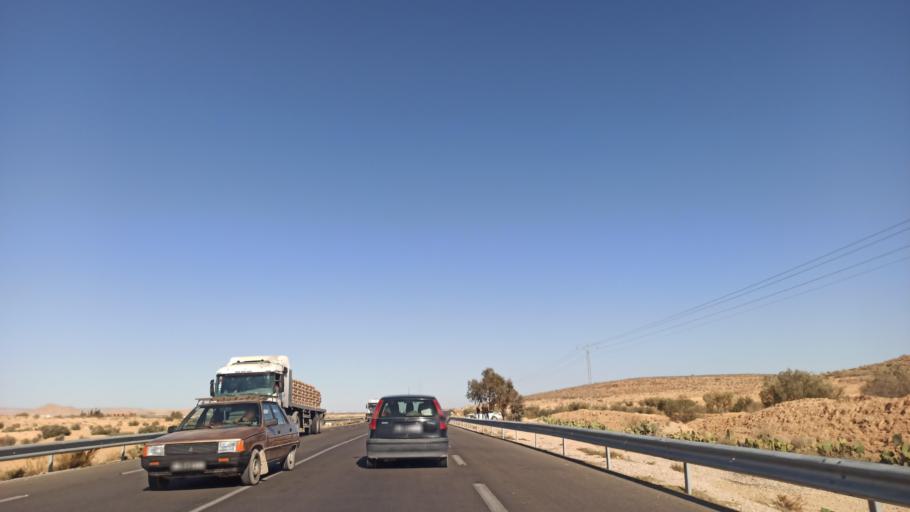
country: TN
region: Sidi Bu Zayd
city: Bi'r al Hufayy
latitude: 34.7206
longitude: 9.0604
